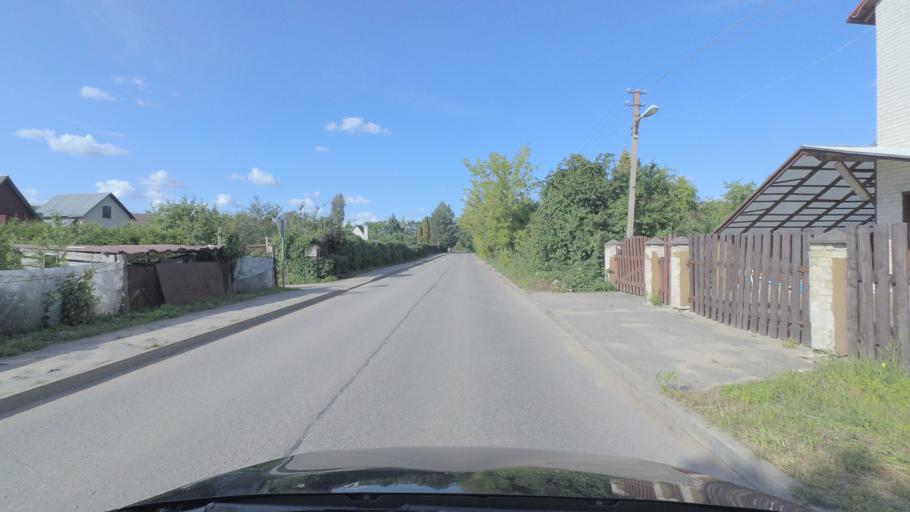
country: LT
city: Nemencine
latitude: 54.8350
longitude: 25.3696
